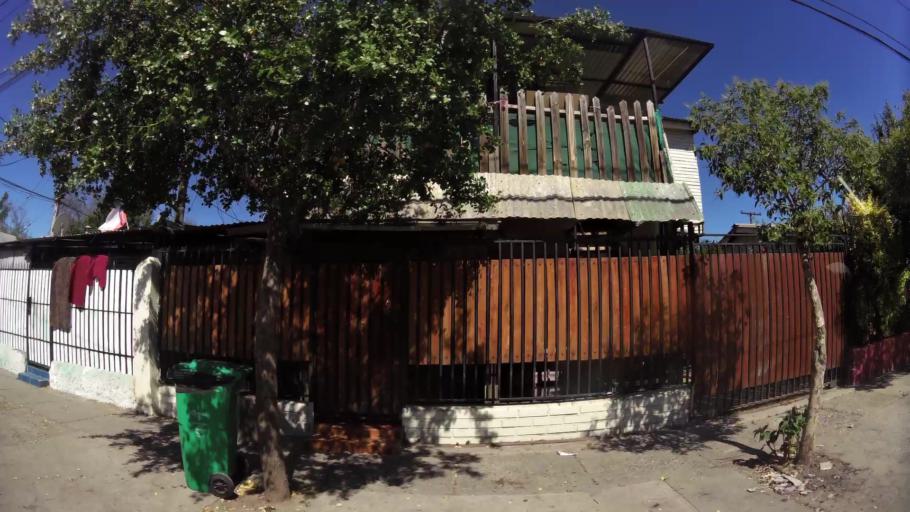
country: CL
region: Santiago Metropolitan
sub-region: Provincia de Maipo
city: San Bernardo
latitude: -33.5853
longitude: -70.6881
